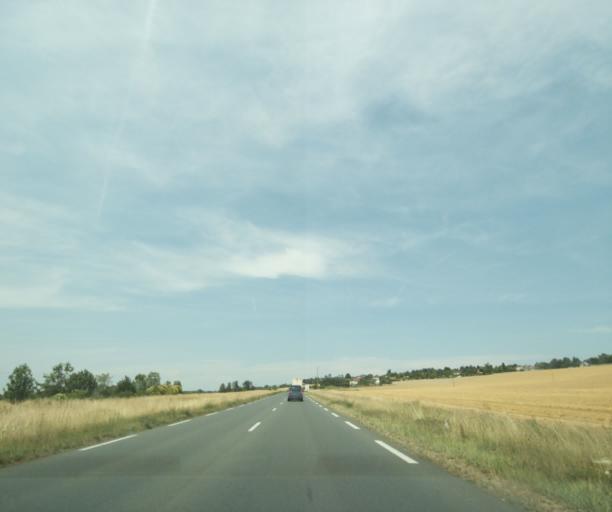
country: FR
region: Poitou-Charentes
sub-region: Departement de la Vienne
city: Chatellerault
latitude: 46.8035
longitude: 0.5639
